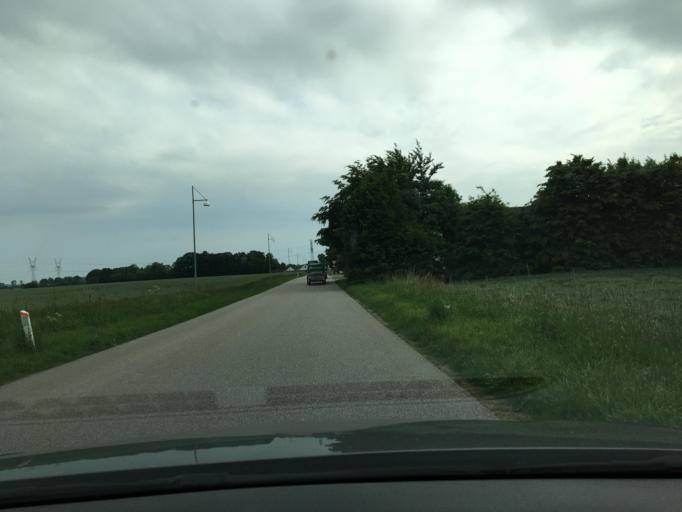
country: DK
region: South Denmark
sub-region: Middelfart Kommune
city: Norre Aby
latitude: 55.4738
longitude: 9.8084
